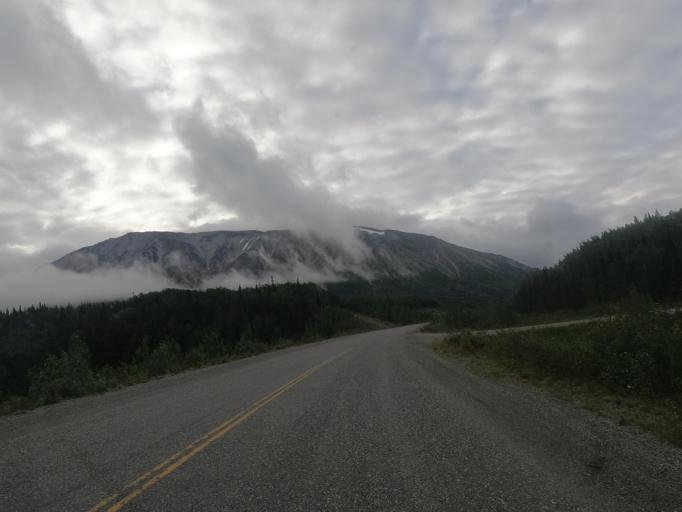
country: CA
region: Yukon
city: Haines Junction
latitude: 60.1104
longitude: -136.9259
